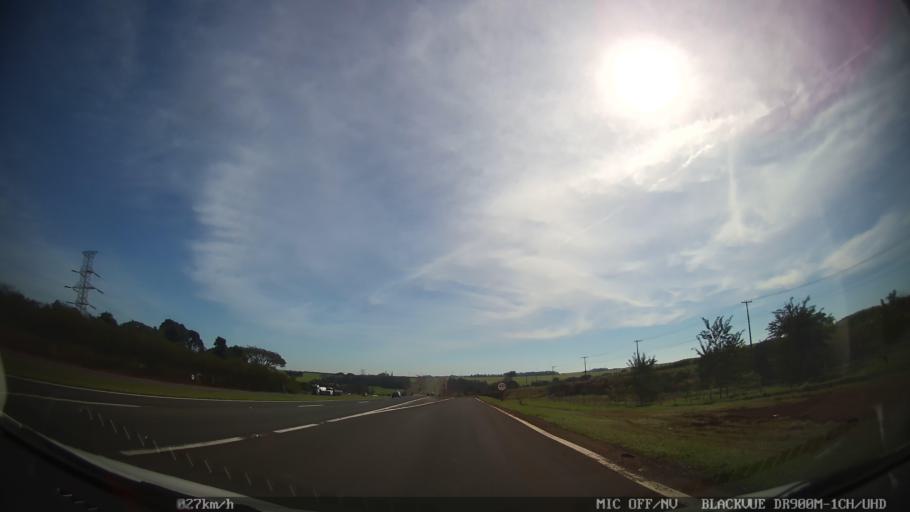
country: BR
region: Sao Paulo
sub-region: Araras
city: Araras
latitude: -22.3154
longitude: -47.3905
